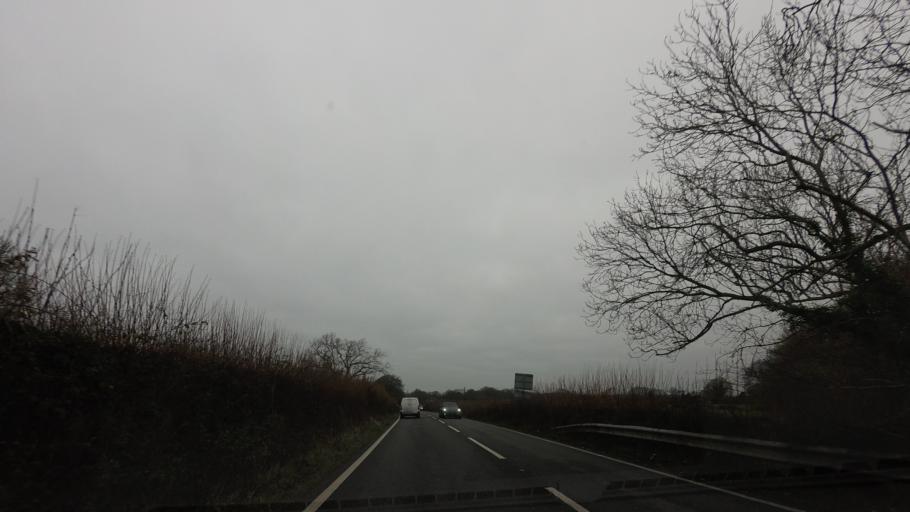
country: GB
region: England
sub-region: East Sussex
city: Saint Leonards-on-Sea
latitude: 50.9035
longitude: 0.5514
